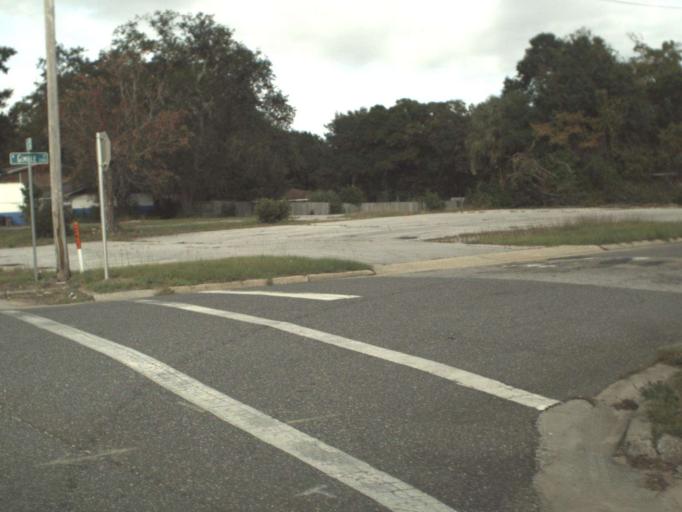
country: US
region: Florida
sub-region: Escambia County
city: Pensacola
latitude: 30.4048
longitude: -87.2421
